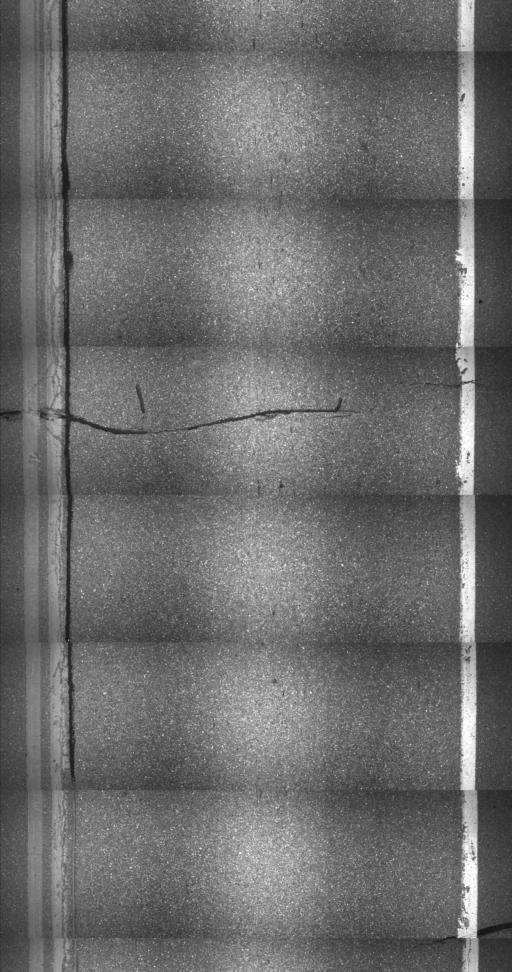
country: US
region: Vermont
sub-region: Chittenden County
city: Milton
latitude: 44.6140
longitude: -73.1524
